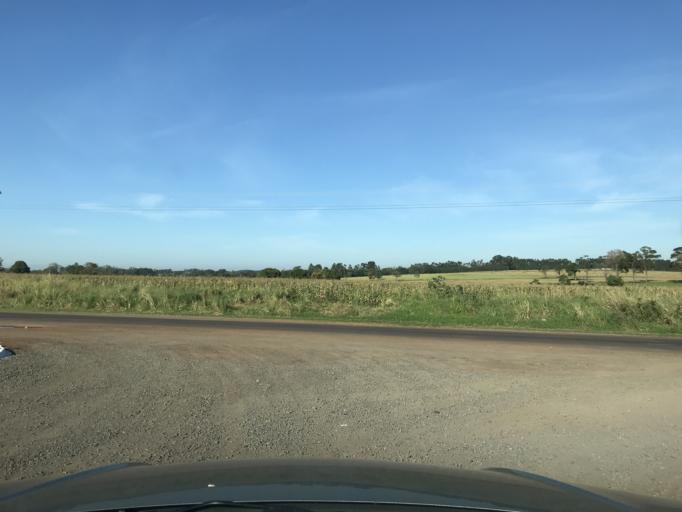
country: BR
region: Parana
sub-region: Ipora
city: Ipora
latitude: -24.0221
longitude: -53.7304
